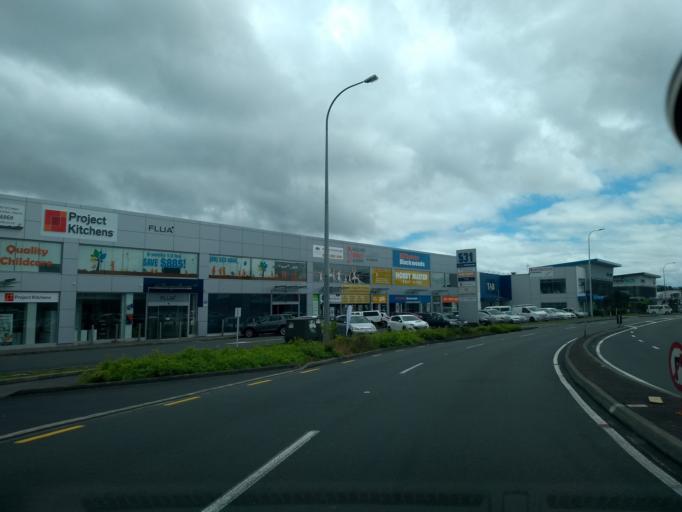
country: NZ
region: Auckland
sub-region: Auckland
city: Tamaki
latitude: -36.9079
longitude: 174.8126
